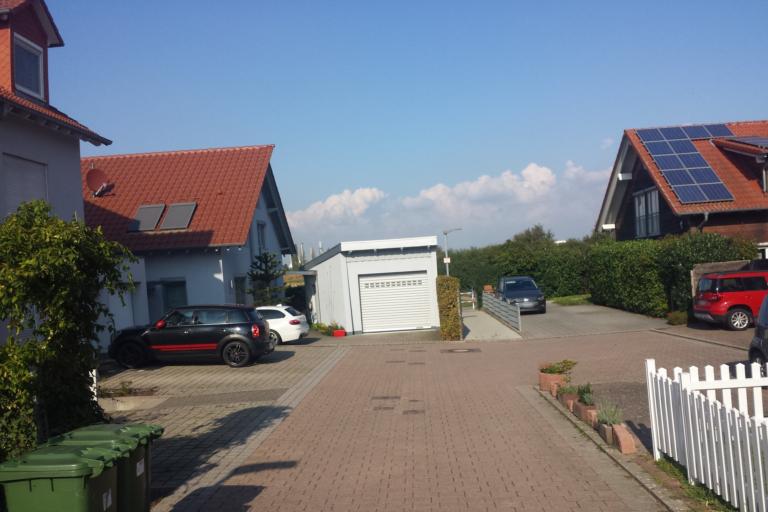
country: DE
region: Baden-Wuerttemberg
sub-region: Karlsruhe Region
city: Ilvesheim
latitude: 49.4758
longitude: 8.5707
